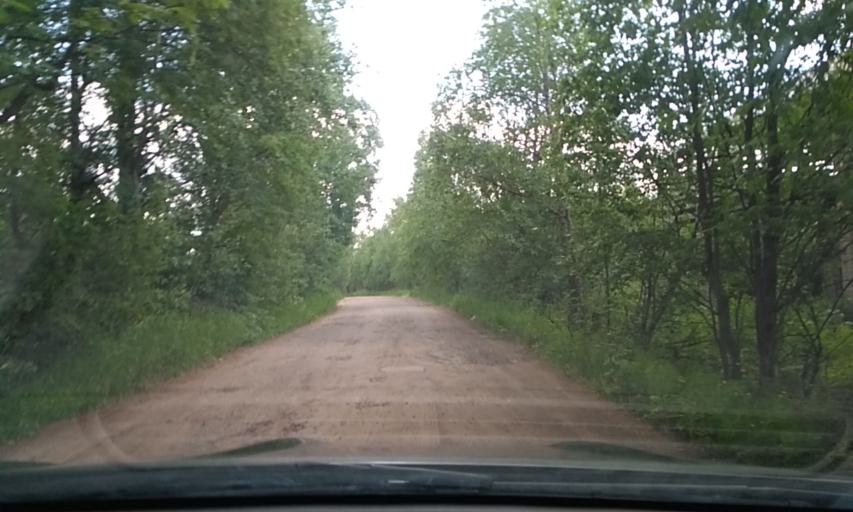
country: RU
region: Leningrad
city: Otradnoye
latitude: 59.8182
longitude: 30.8254
